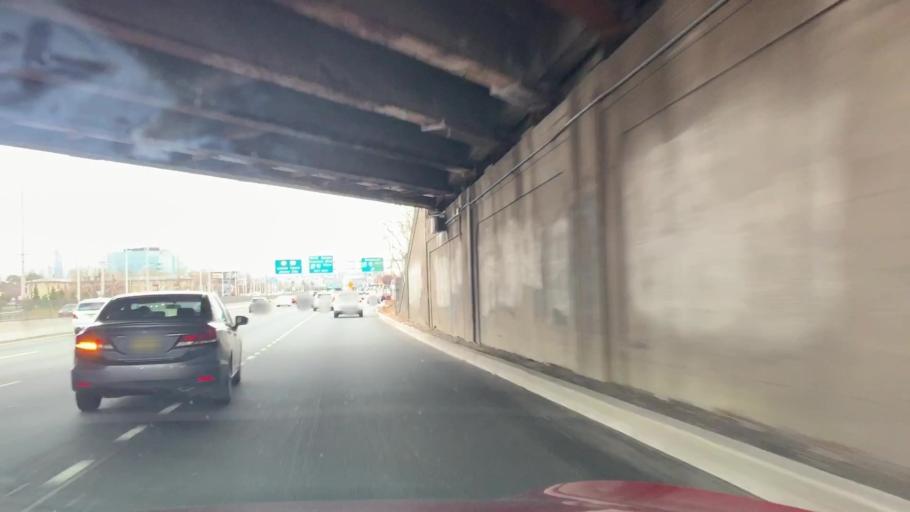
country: US
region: New Jersey
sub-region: Hudson County
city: Secaucus
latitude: 40.7942
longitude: -74.0585
